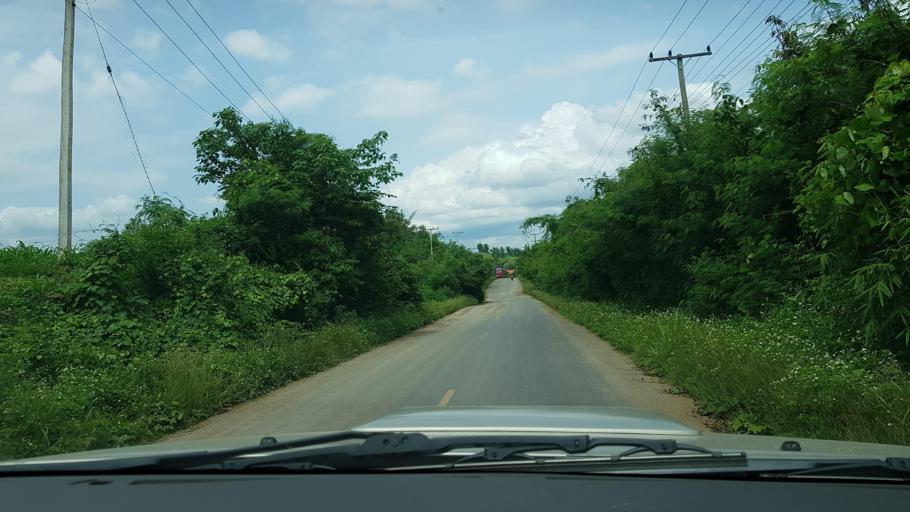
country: TH
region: Nan
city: Chaloem Phra Kiat
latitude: 20.0218
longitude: 101.3263
